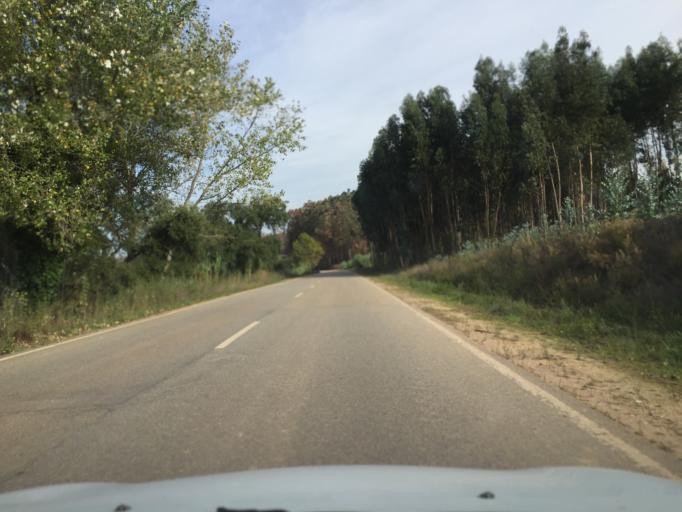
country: PT
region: Aveiro
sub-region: Anadia
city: Anadia
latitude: 40.4204
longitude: -8.4131
